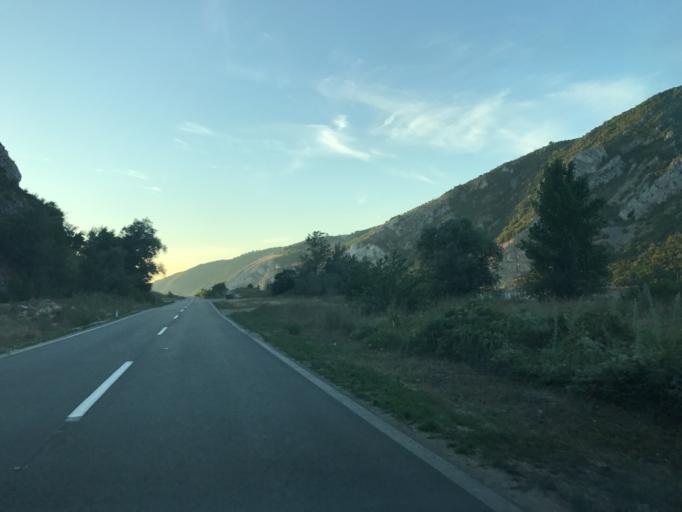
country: RO
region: Caras-Severin
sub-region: Comuna Pescari
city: Coronini
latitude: 44.6572
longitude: 21.7043
